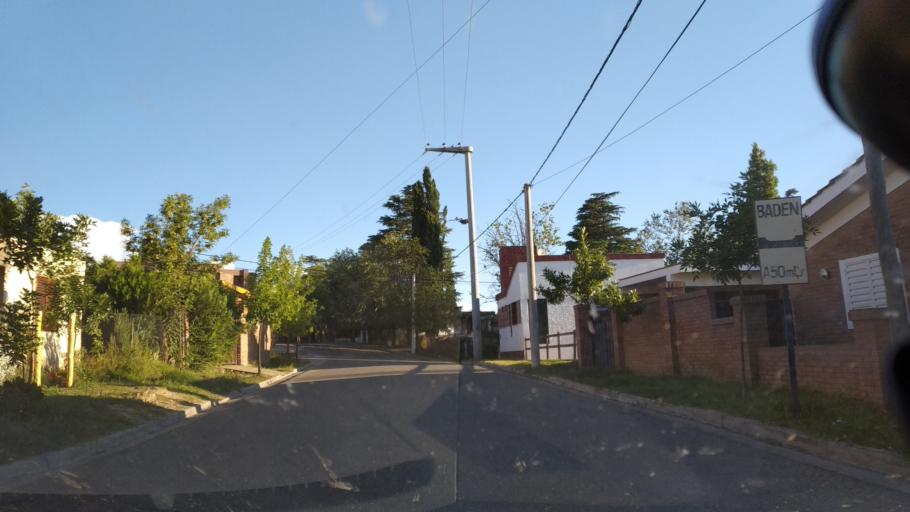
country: AR
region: Cordoba
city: Mina Clavero
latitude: -31.7189
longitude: -65.0026
